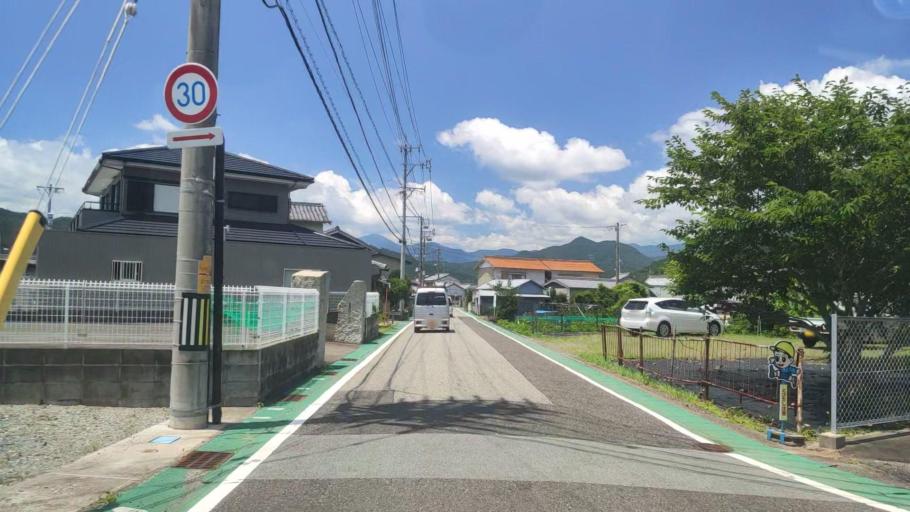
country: JP
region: Mie
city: Owase
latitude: 34.2072
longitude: 136.3430
